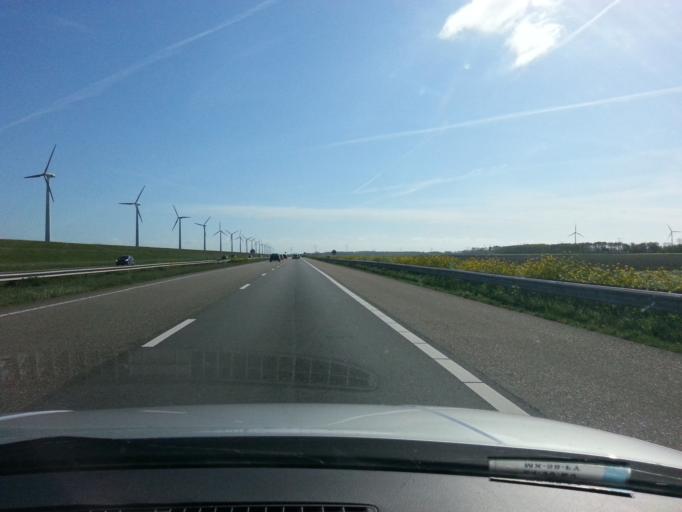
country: NL
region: Flevoland
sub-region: Gemeente Urk
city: Urk
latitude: 52.5950
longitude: 5.5728
